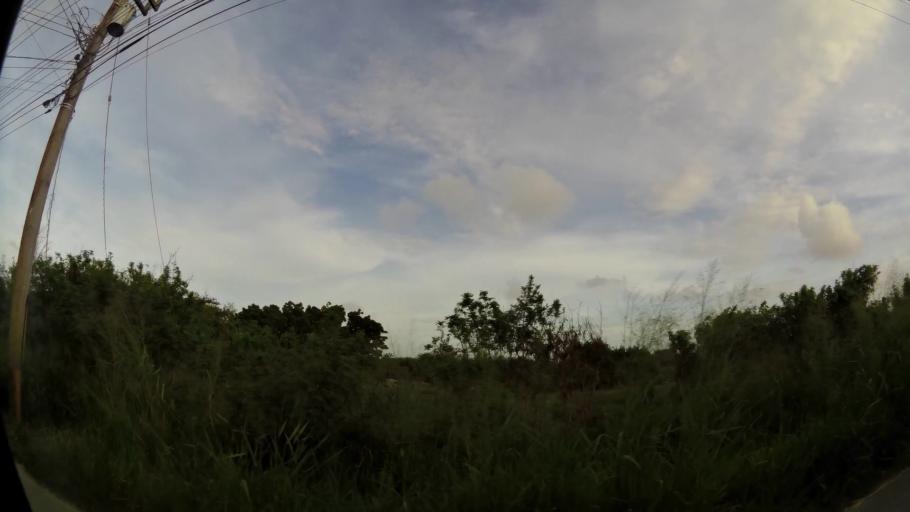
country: BB
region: Saint Philip
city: Crane
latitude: 13.0861
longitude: -59.4925
